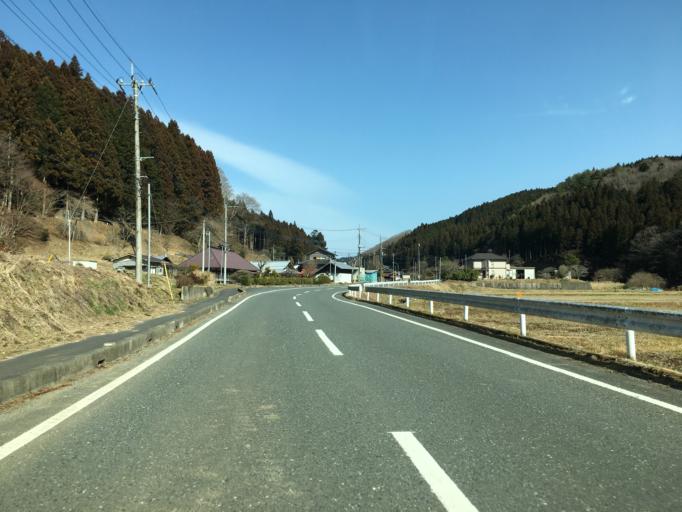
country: JP
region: Ibaraki
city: Daigo
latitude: 36.8190
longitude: 140.5197
